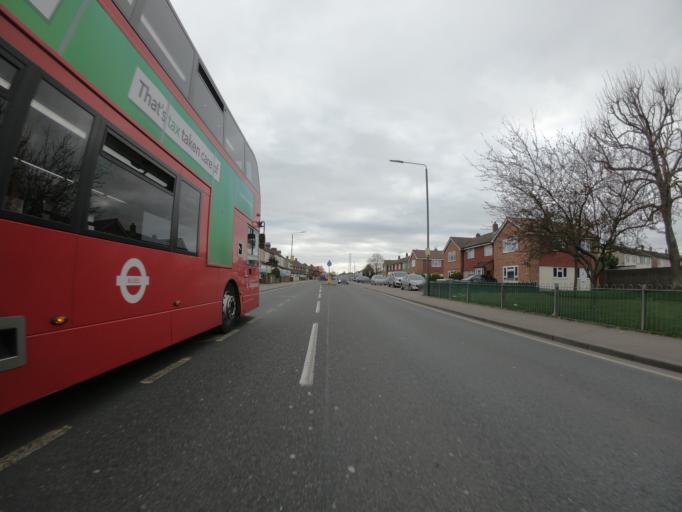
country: GB
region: England
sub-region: Greater London
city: Welling
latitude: 51.4708
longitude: 0.1106
